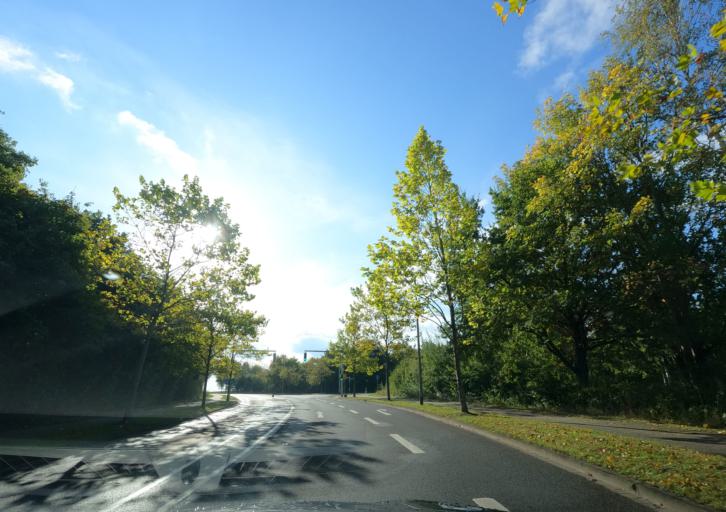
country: DE
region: Lower Saxony
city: Leiferde
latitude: 52.2317
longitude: 10.4879
